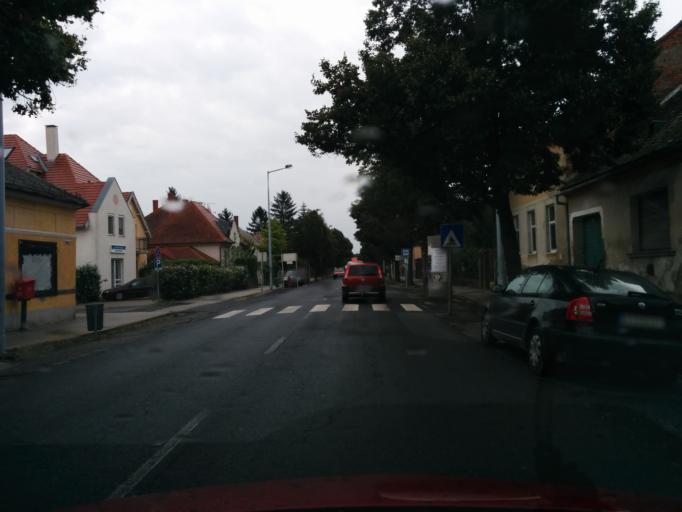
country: HU
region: Vas
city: Koszeg
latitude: 47.3825
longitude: 16.5510
